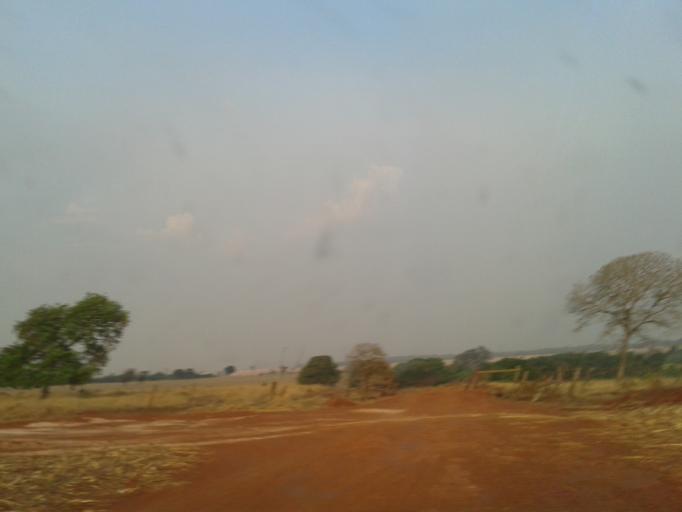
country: BR
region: Minas Gerais
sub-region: Capinopolis
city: Capinopolis
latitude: -18.8077
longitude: -49.7358
